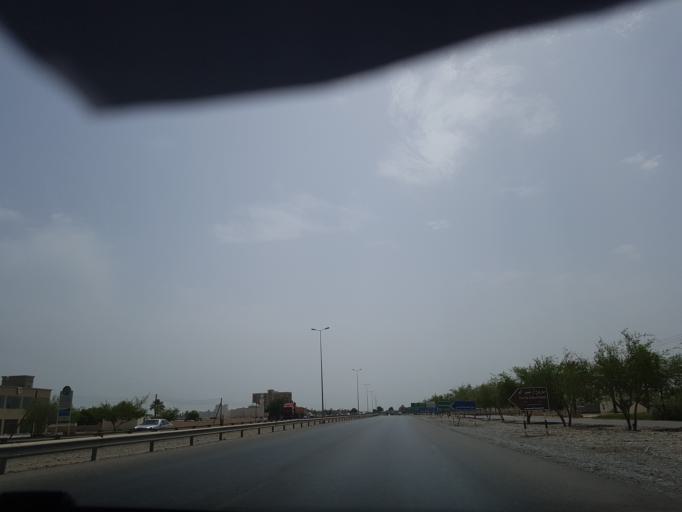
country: OM
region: Al Batinah
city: As Suwayq
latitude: 23.7408
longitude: 57.6389
